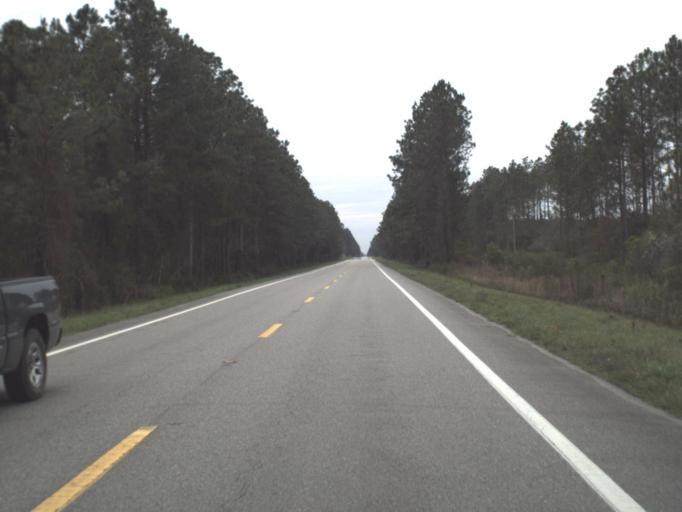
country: US
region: Florida
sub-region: Gulf County
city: Wewahitchka
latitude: 29.9433
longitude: -85.1859
